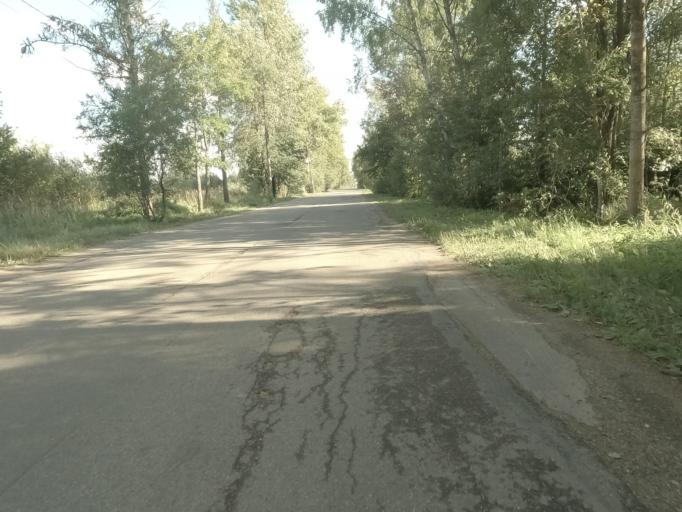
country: RU
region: Leningrad
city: Imeni Morozova
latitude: 59.9700
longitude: 31.0277
